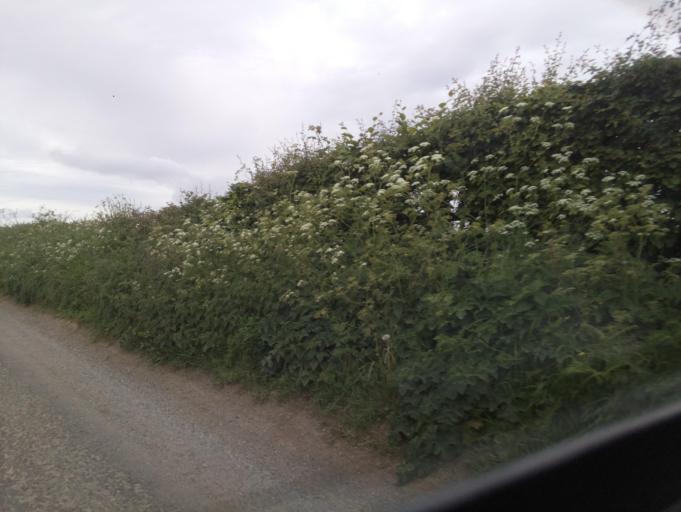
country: GB
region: England
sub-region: Devon
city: Dartmouth
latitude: 50.3250
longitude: -3.6396
